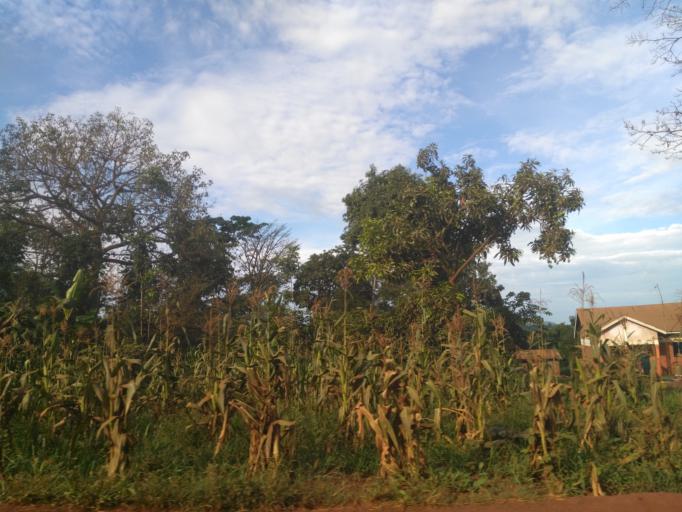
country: UG
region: Eastern Region
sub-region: Jinja District
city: Jinja
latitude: 0.4686
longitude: 33.1735
